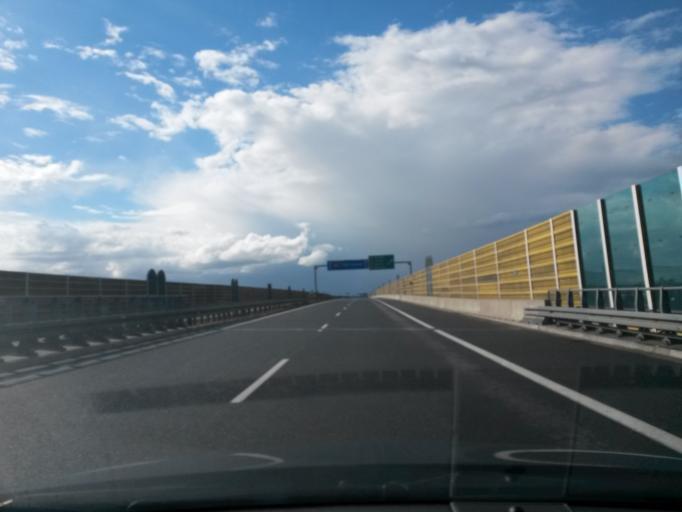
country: PL
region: Greater Poland Voivodeship
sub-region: Powiat wrzesinski
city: Wrzesnia
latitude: 52.3124
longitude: 17.5494
